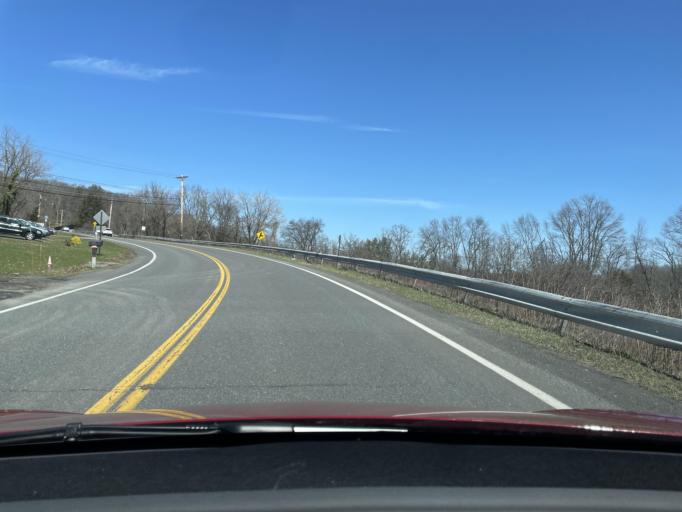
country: US
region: New York
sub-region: Ulster County
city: Lincoln Park
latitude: 41.9512
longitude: -74.0191
